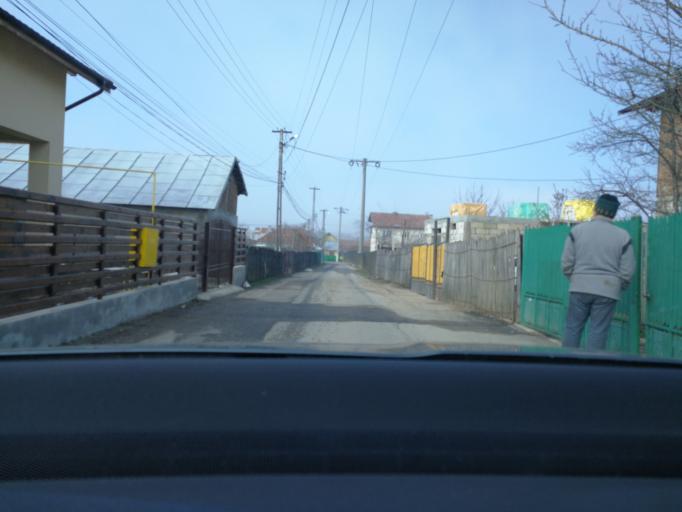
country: RO
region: Prahova
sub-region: Comuna Magureni
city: Magureni
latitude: 45.0510
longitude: 25.7492
